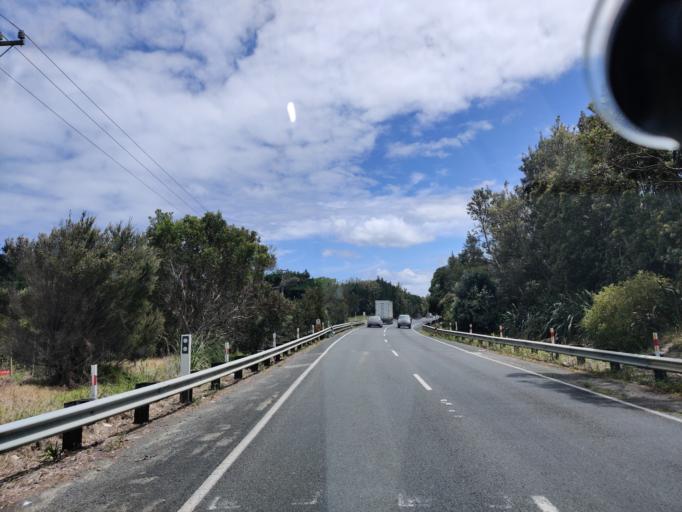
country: NZ
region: Northland
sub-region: Far North District
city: Kaitaia
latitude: -34.8344
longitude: 173.1318
